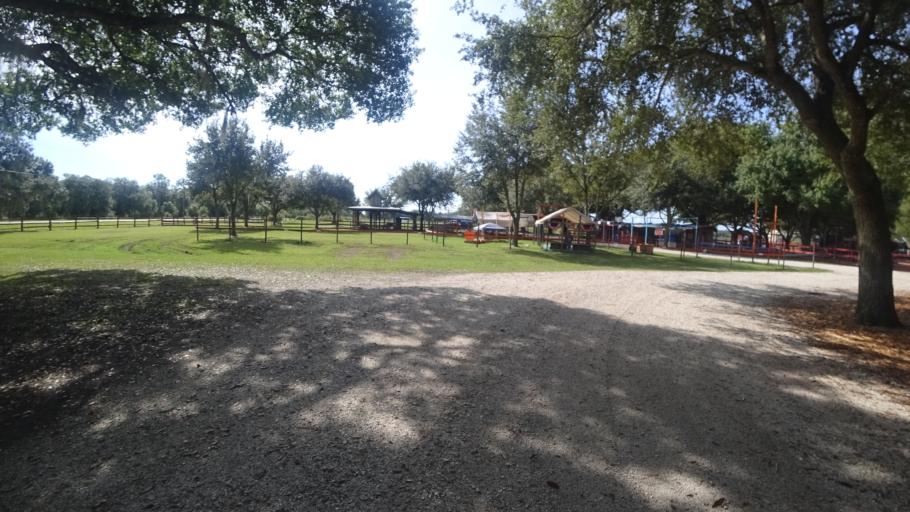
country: US
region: Florida
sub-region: Sarasota County
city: The Meadows
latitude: 27.4445
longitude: -82.3039
